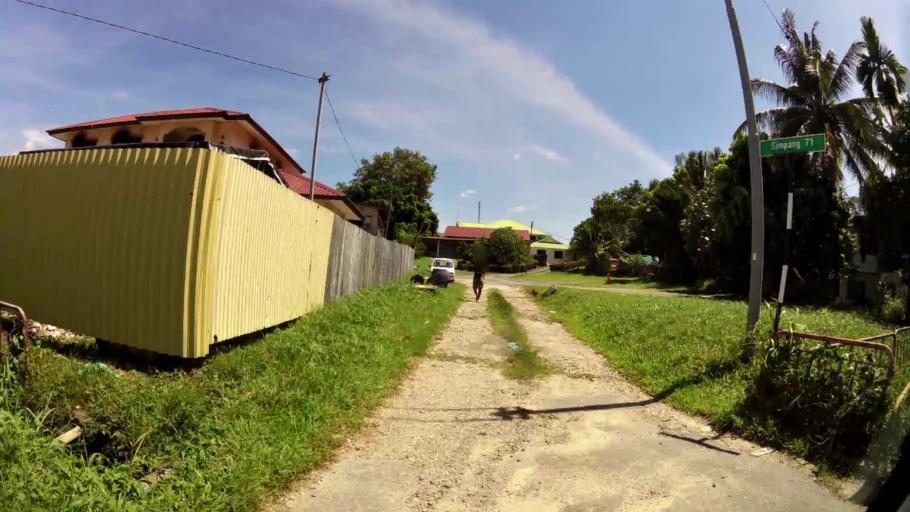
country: BN
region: Brunei and Muara
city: Bandar Seri Begawan
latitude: 4.9408
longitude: 114.9471
